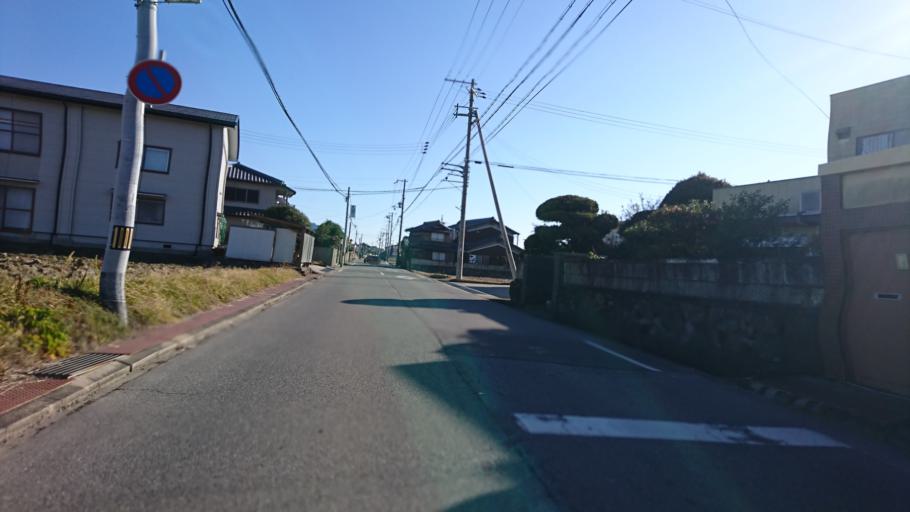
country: JP
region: Hyogo
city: Kakogawacho-honmachi
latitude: 34.7524
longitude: 134.8839
